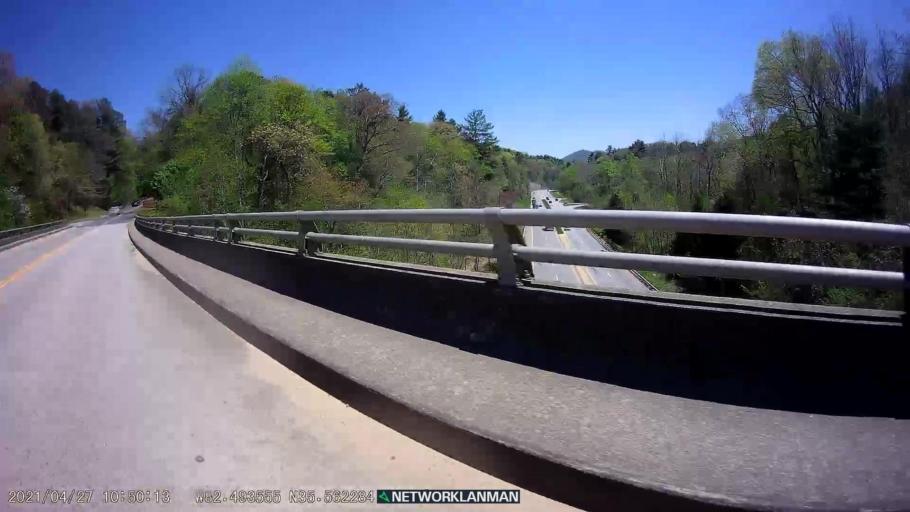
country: US
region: North Carolina
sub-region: Buncombe County
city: Biltmore Forest
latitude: 35.5638
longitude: -82.4918
